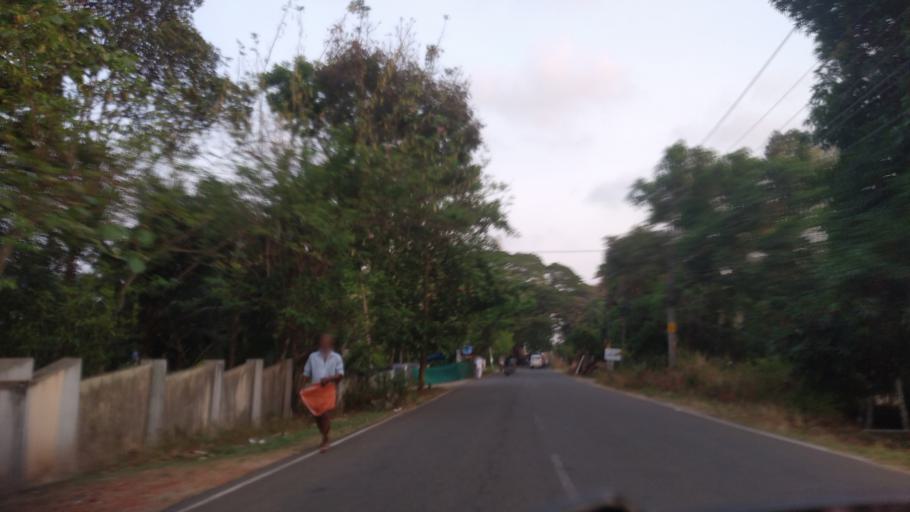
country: IN
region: Kerala
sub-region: Thrissur District
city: Kodungallur
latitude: 10.2191
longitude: 76.1593
